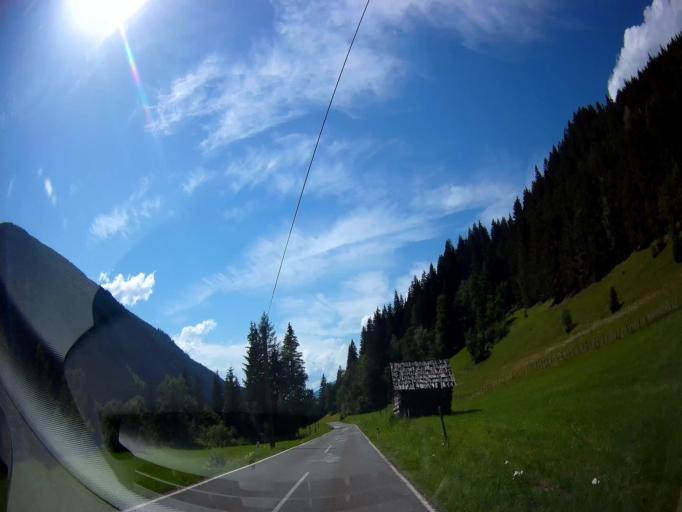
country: AT
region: Salzburg
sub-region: Politischer Bezirk Tamsweg
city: Thomatal
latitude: 47.0647
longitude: 13.7674
